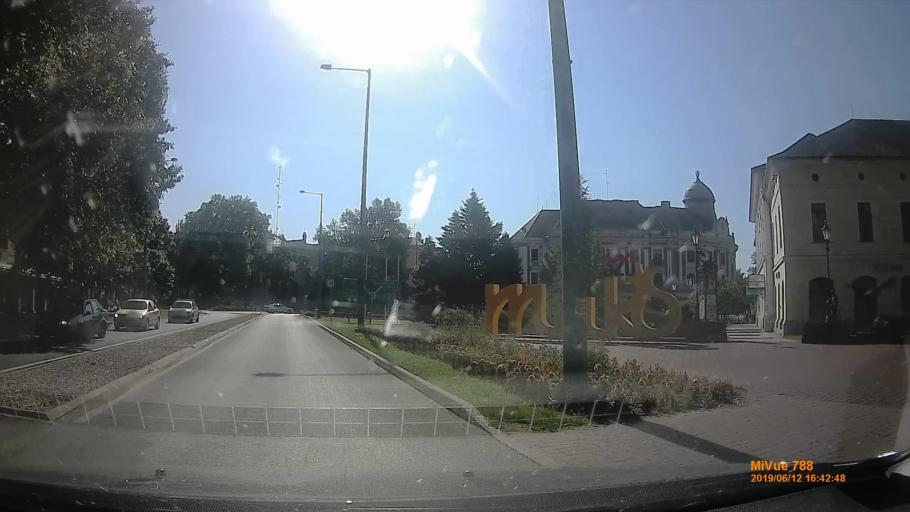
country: HU
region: Csongrad
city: Mako
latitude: 46.2150
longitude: 20.4758
